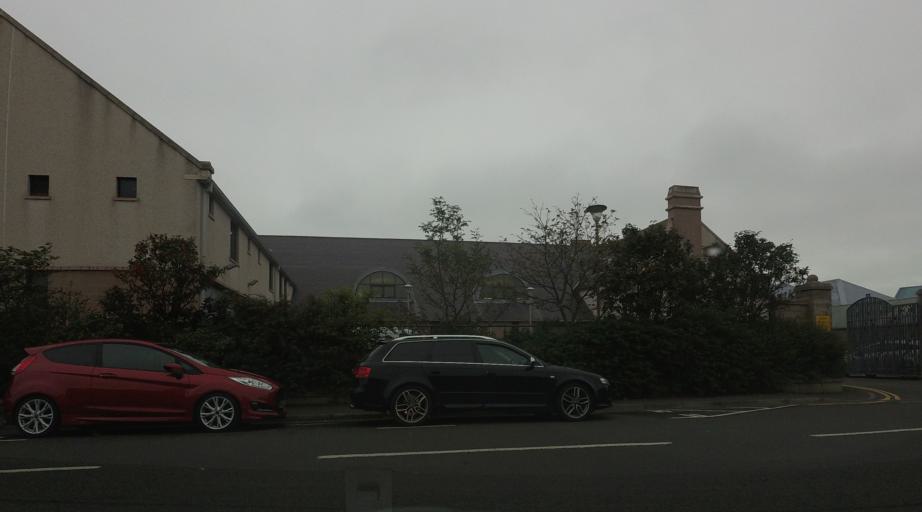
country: GB
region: Scotland
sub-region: Orkney Islands
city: Orkney
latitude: 58.9824
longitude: -2.9640
